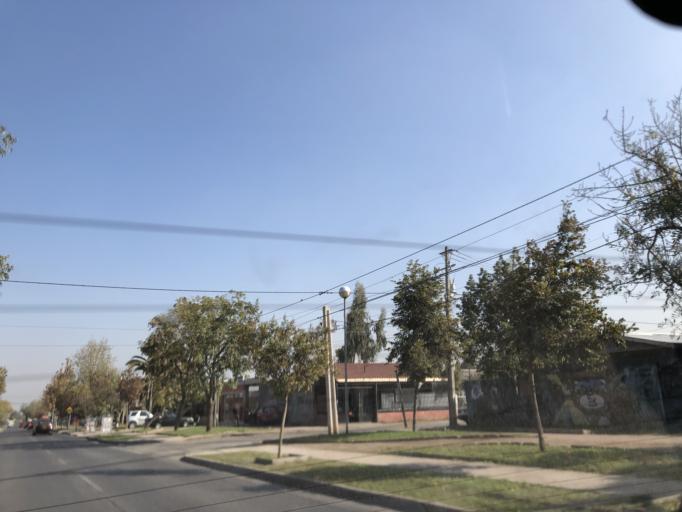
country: CL
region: Santiago Metropolitan
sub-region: Provincia de Cordillera
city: Puente Alto
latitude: -33.6175
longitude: -70.5827
